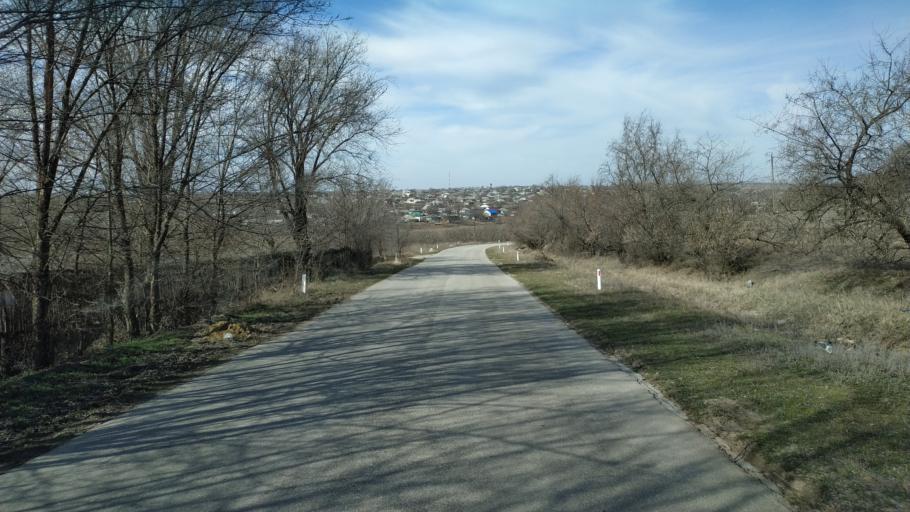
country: MD
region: Nisporeni
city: Nisporeni
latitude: 46.9549
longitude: 28.2239
